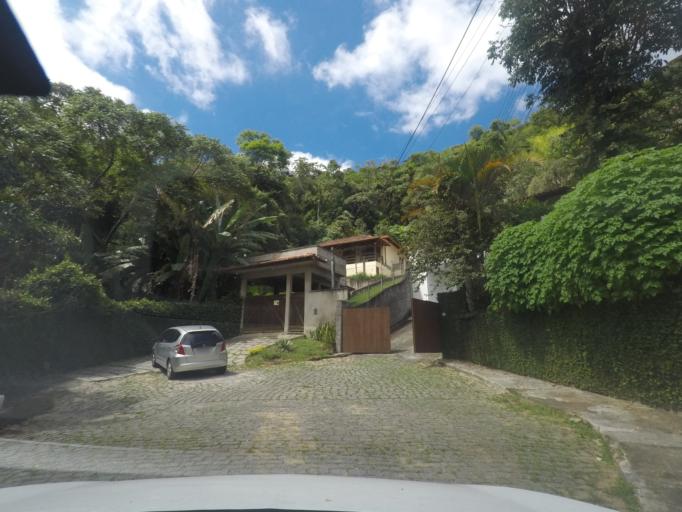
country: BR
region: Rio de Janeiro
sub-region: Teresopolis
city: Teresopolis
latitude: -22.4002
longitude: -42.9849
